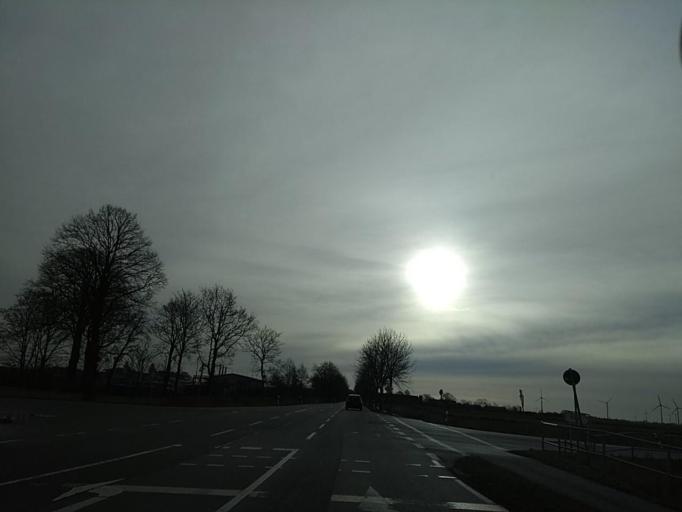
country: DE
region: Lower Saxony
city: Jemgum
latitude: 53.2567
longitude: 7.3855
